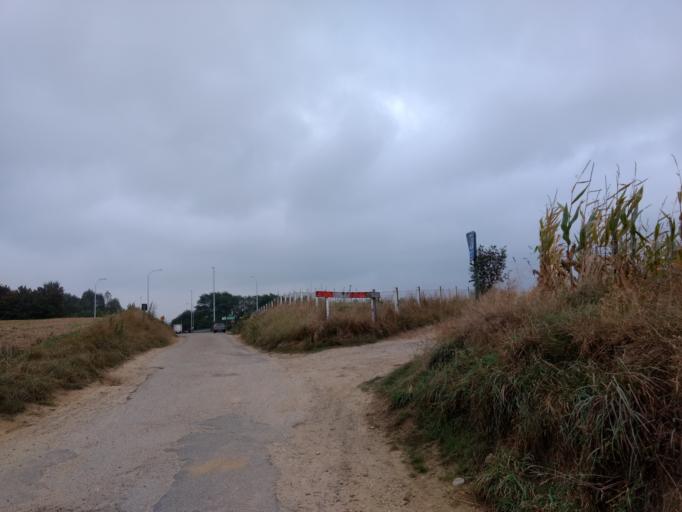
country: BE
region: Flanders
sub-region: Provincie Vlaams-Brabant
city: Herent
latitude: 50.8791
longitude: 4.6614
